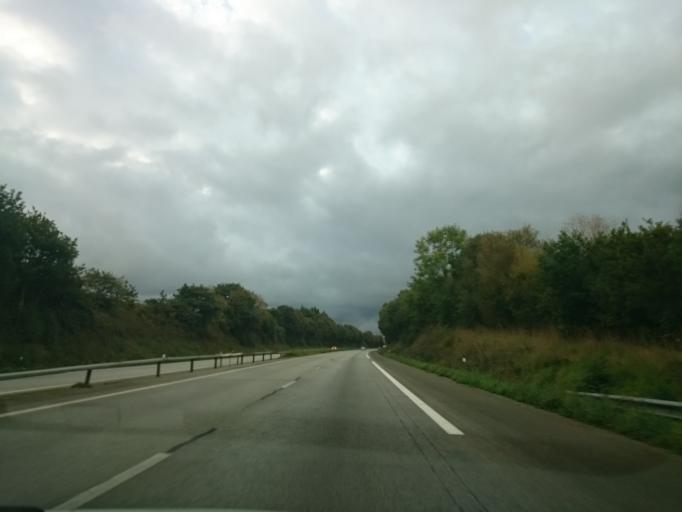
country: FR
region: Brittany
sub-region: Departement du Finistere
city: Briec
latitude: 48.1317
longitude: -4.0248
